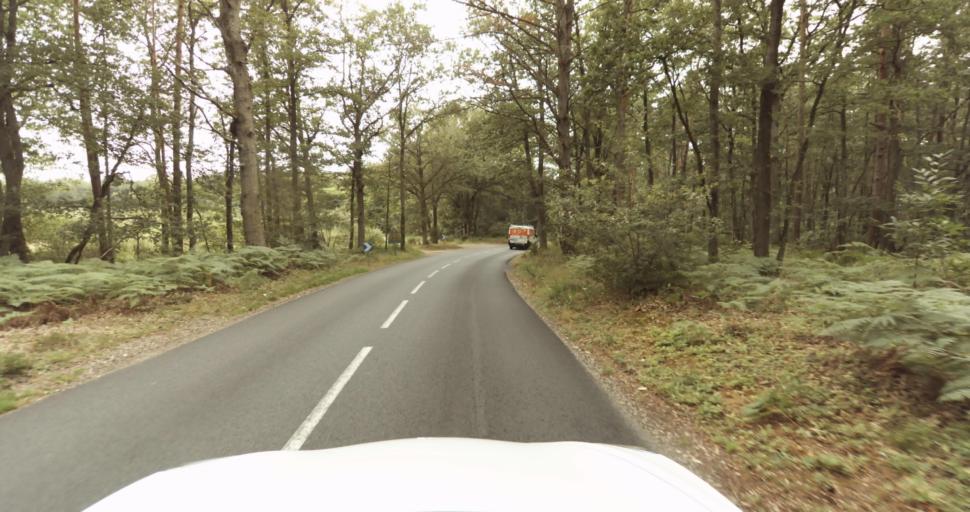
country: FR
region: Haute-Normandie
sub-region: Departement de l'Eure
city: Saint-Sebastien-de-Morsent
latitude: 48.9886
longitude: 1.0568
